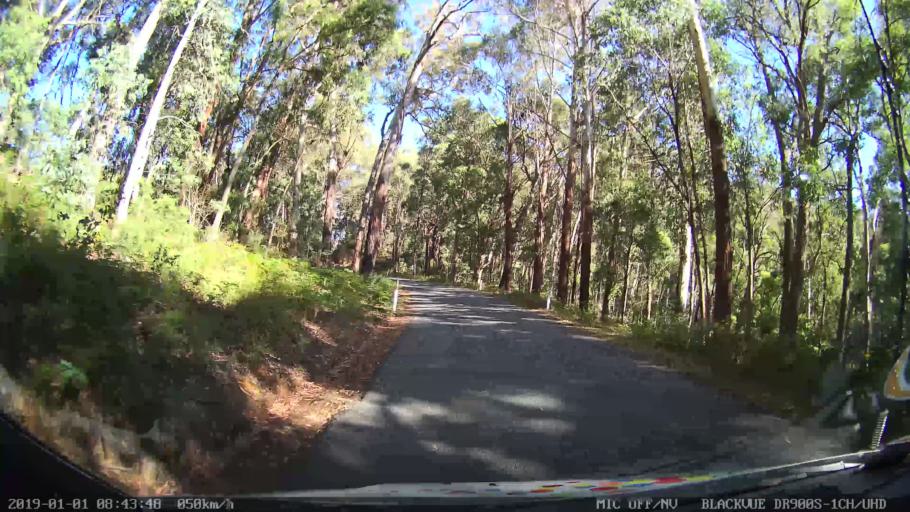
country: AU
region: New South Wales
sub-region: Snowy River
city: Jindabyne
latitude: -36.3147
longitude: 148.1919
